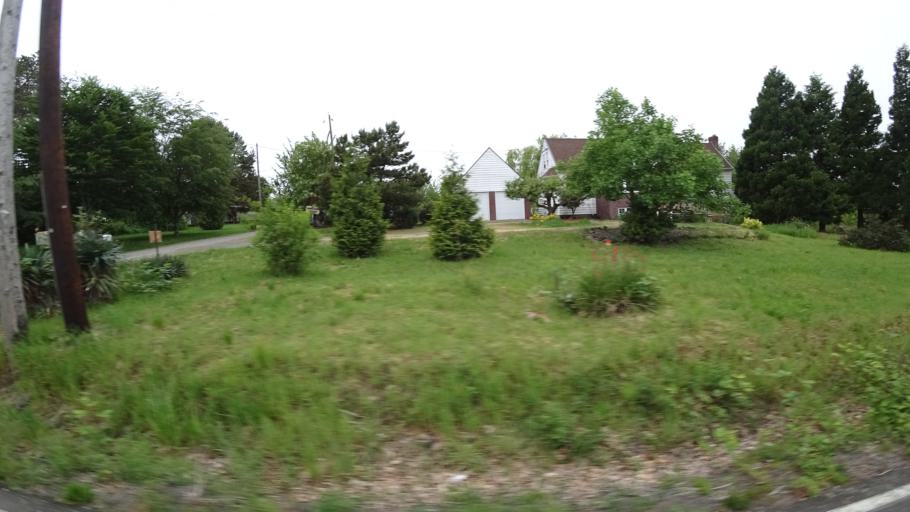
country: US
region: Oregon
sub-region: Washington County
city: Bethany
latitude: 45.5506
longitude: -122.8574
